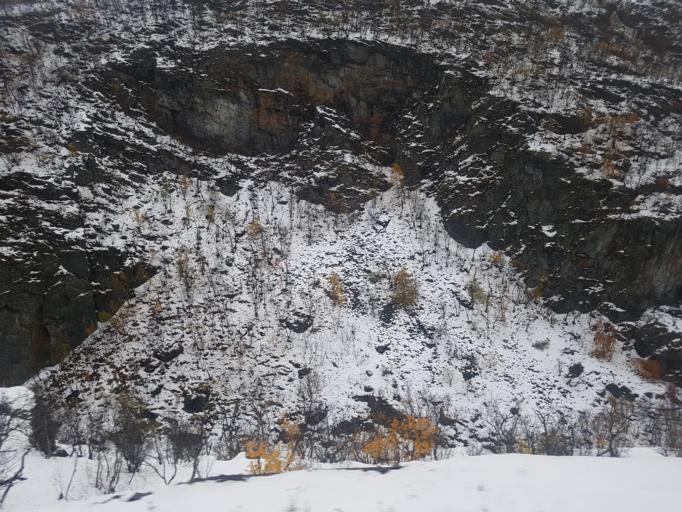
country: NO
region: Sor-Trondelag
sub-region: Oppdal
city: Oppdal
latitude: 62.3445
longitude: 9.6253
